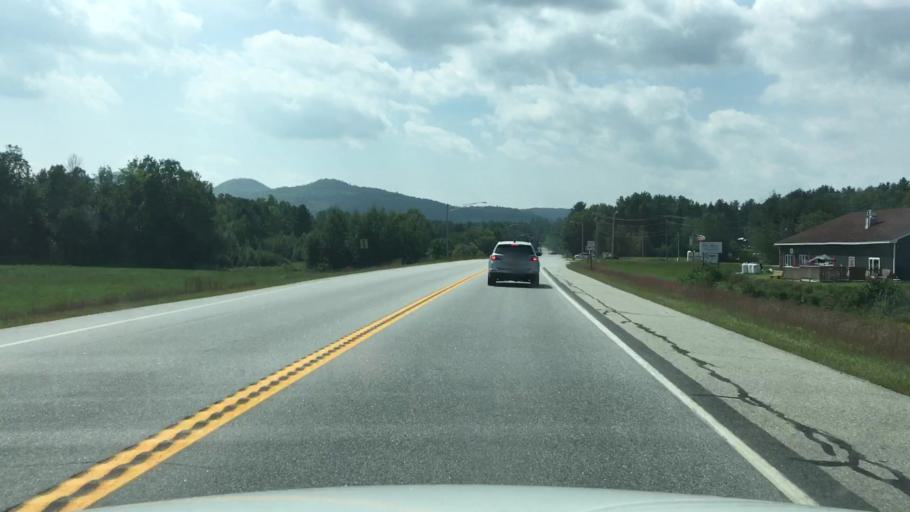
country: US
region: Maine
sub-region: Oxford County
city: Rumford
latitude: 44.5206
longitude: -70.5530
